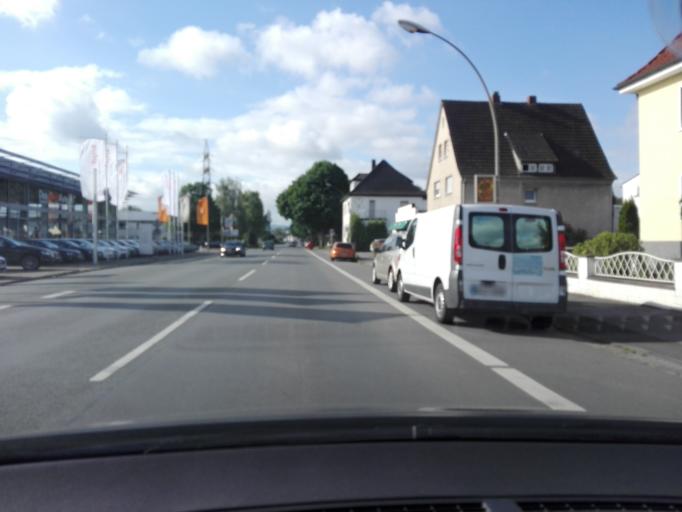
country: DE
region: North Rhine-Westphalia
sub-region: Regierungsbezirk Arnsberg
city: Menden
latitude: 51.4561
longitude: 7.7769
